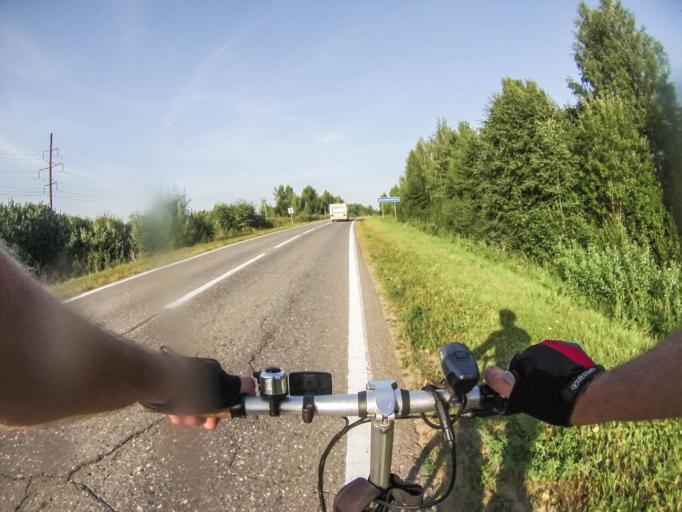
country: RU
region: Jaroslavl
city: Myshkin
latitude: 57.7054
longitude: 38.3587
